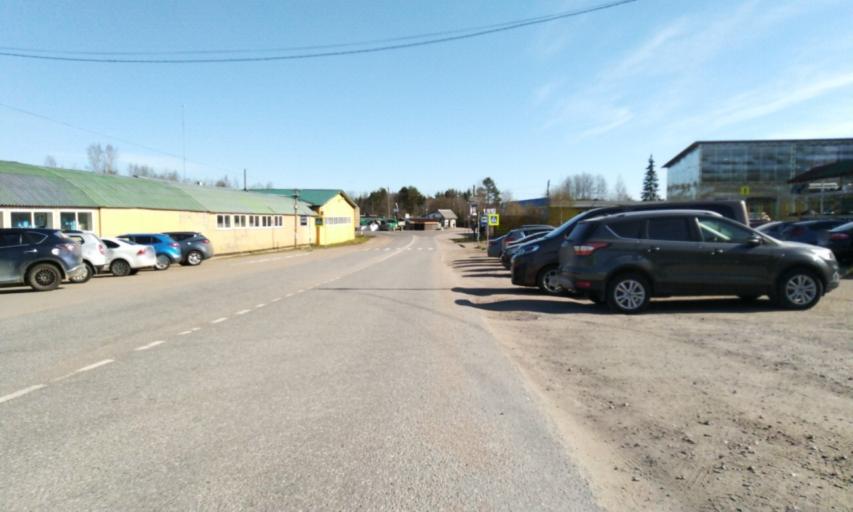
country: RU
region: Leningrad
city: Garbolovo
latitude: 60.3294
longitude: 30.4250
